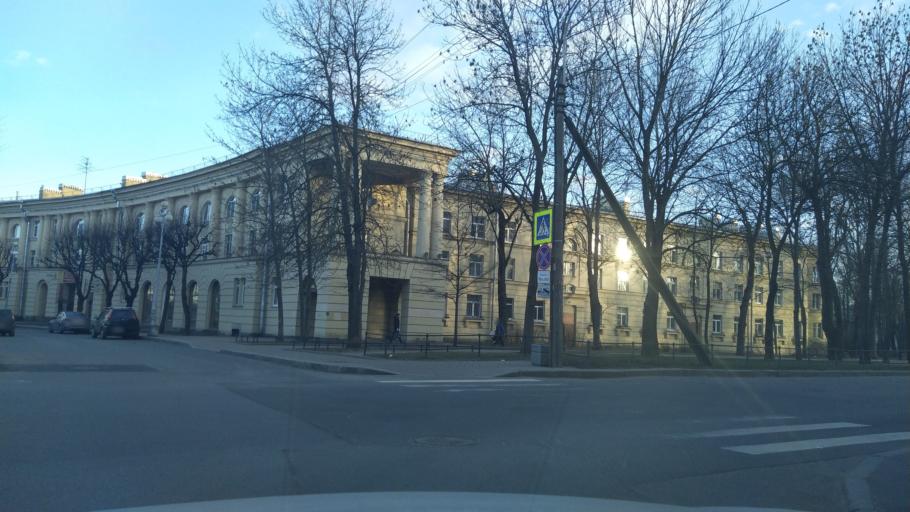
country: RU
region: St.-Petersburg
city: Pushkin
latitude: 59.7222
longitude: 30.4274
